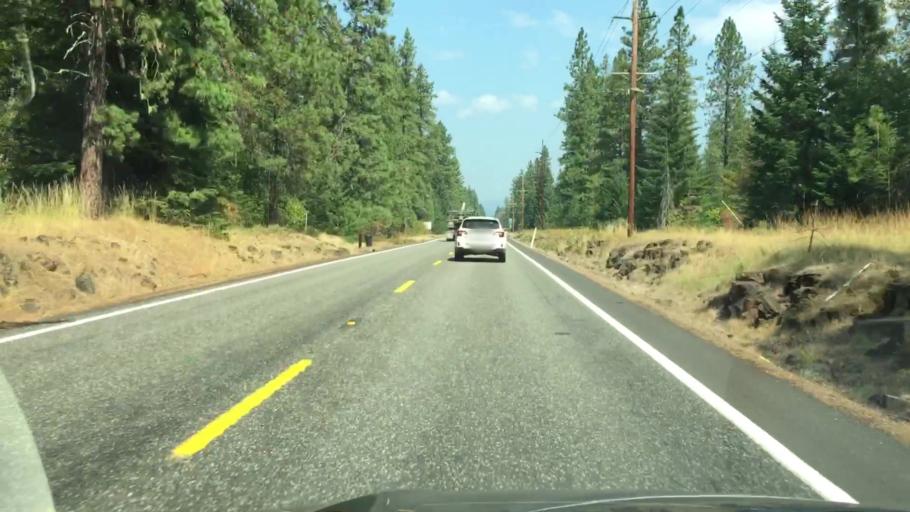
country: US
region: Washington
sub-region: Klickitat County
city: White Salmon
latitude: 45.9203
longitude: -121.4981
